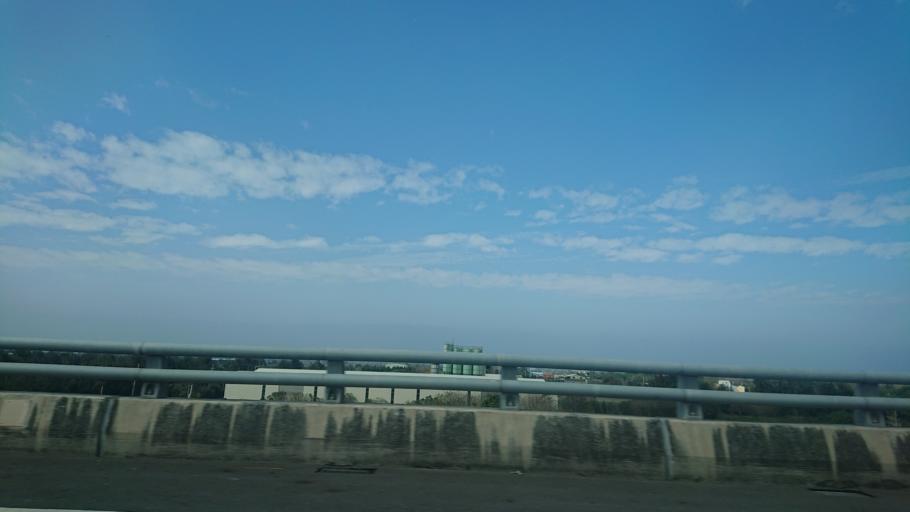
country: TW
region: Taiwan
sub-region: Yunlin
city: Douliu
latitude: 23.8536
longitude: 120.2959
